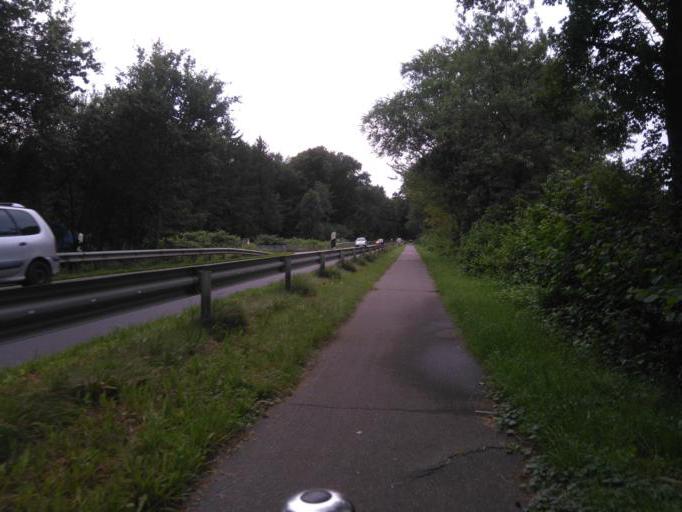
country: DE
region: Schleswig-Holstein
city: Bullenkuhlen
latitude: 53.7781
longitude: 9.7589
